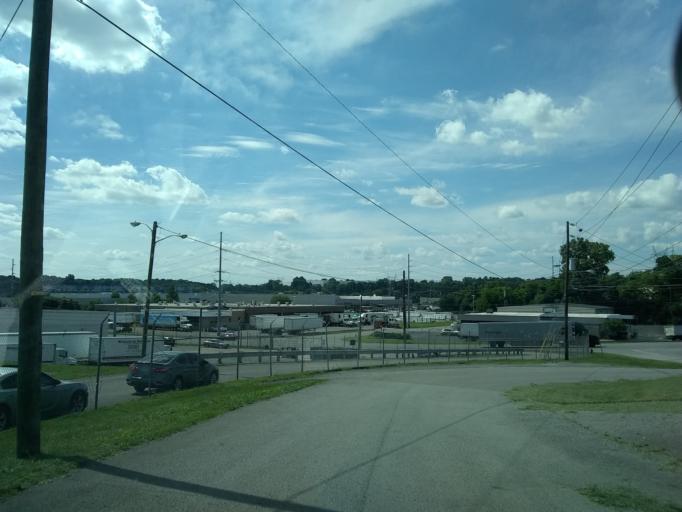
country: US
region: Tennessee
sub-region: Davidson County
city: Nashville
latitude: 36.1448
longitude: -86.7054
